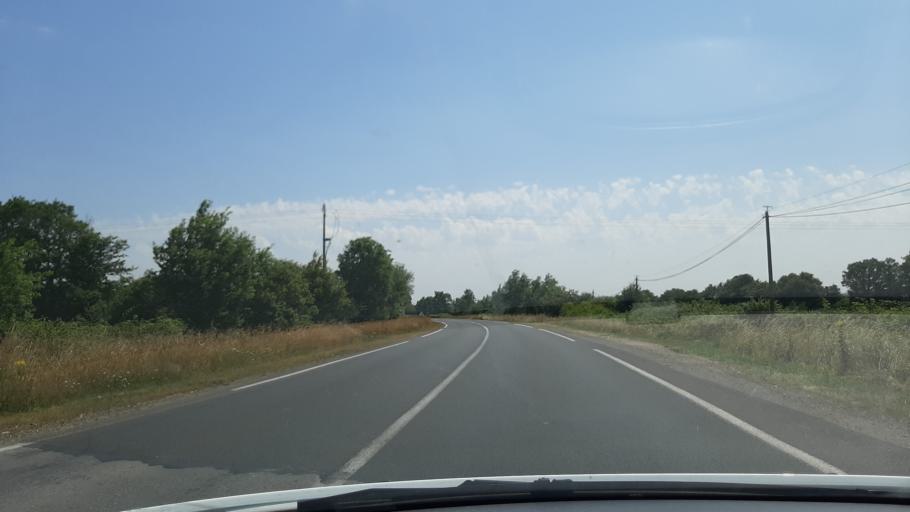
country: FR
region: Pays de la Loire
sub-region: Departement de la Vendee
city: Mouilleron-le-Captif
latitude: 46.7439
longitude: -1.4462
